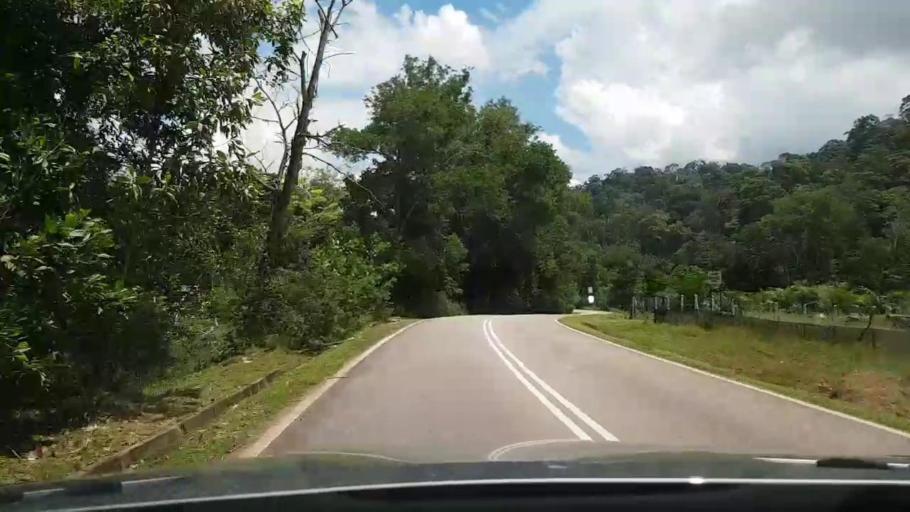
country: MY
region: Pahang
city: Pekan
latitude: 3.1540
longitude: 102.9718
